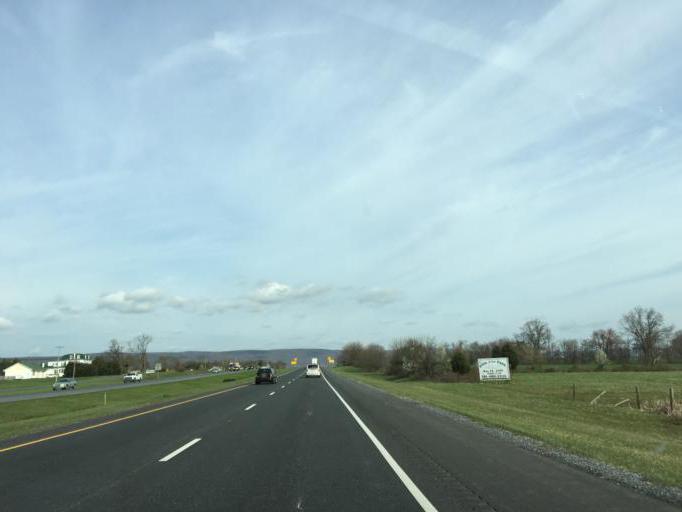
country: US
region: Maryland
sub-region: Frederick County
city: Clover Hill
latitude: 39.5120
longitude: -77.4080
